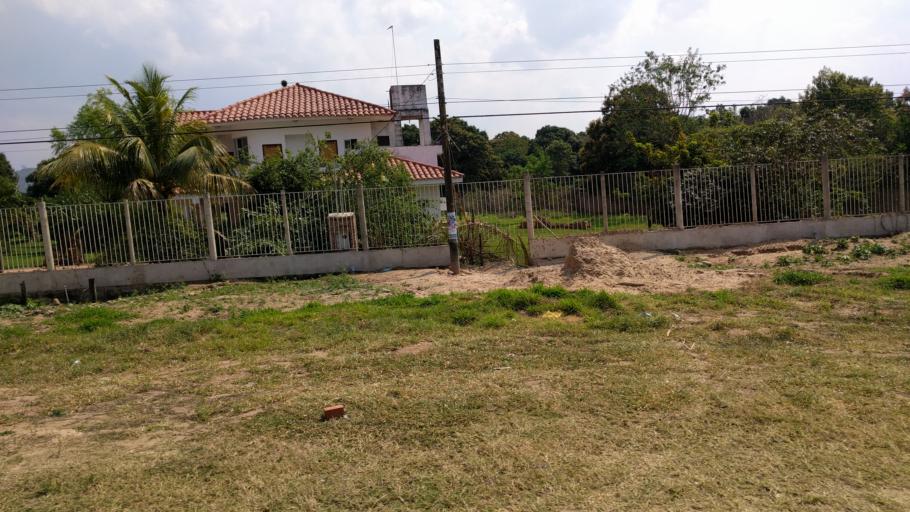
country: BO
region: Santa Cruz
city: Santa Rita
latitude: -17.9630
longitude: -63.3618
